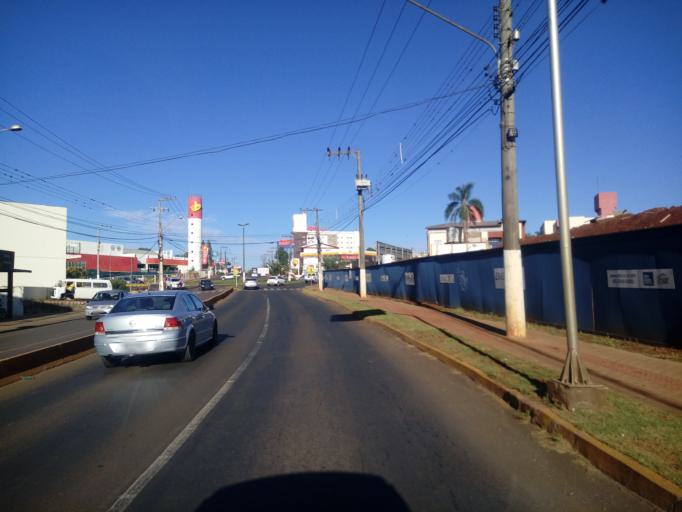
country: BR
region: Santa Catarina
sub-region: Chapeco
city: Chapeco
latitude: -27.0945
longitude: -52.6363
